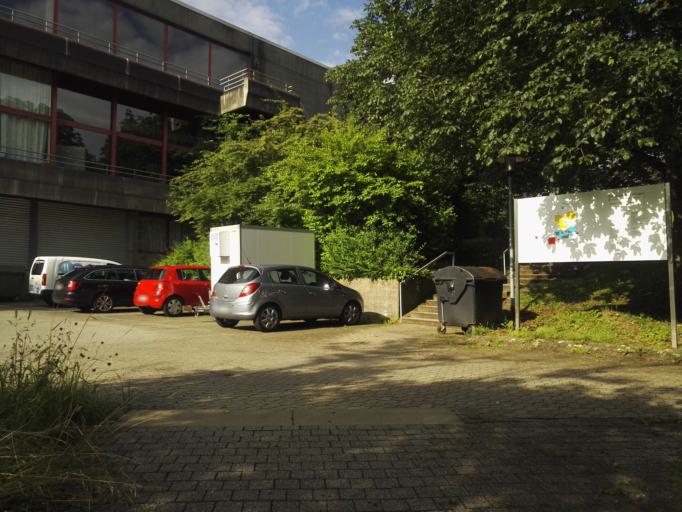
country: DE
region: Baden-Wuerttemberg
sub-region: Regierungsbezirk Stuttgart
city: Esslingen
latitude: 48.7450
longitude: 9.3240
